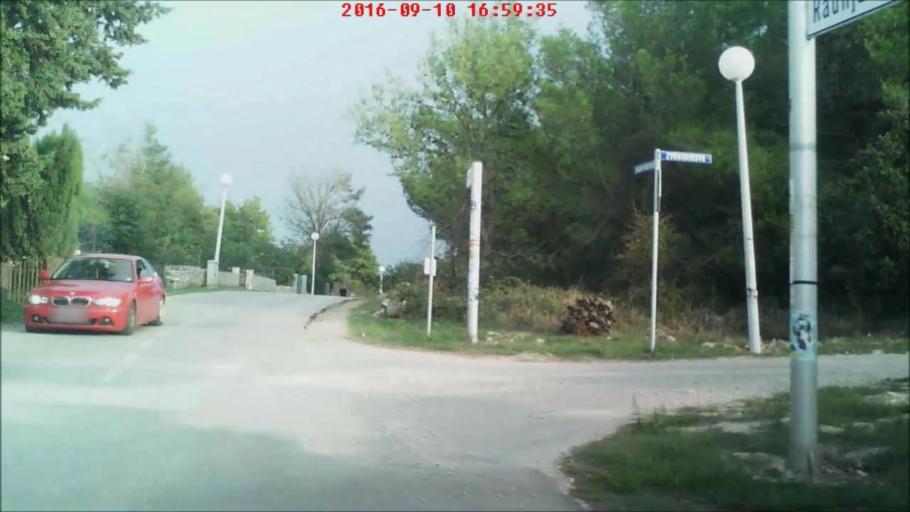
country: HR
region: Zadarska
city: Vir
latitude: 44.3121
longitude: 15.0546
